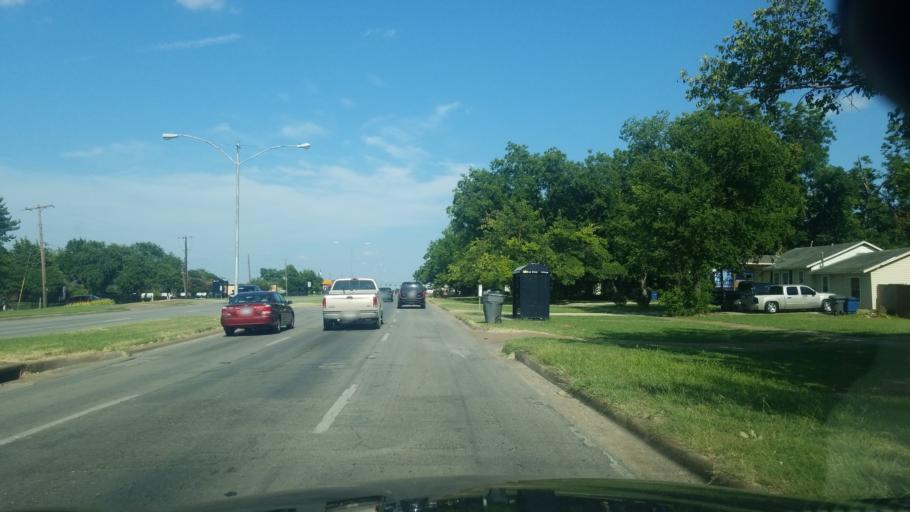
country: US
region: Texas
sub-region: Dallas County
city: Dallas
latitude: 32.7168
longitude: -96.7823
